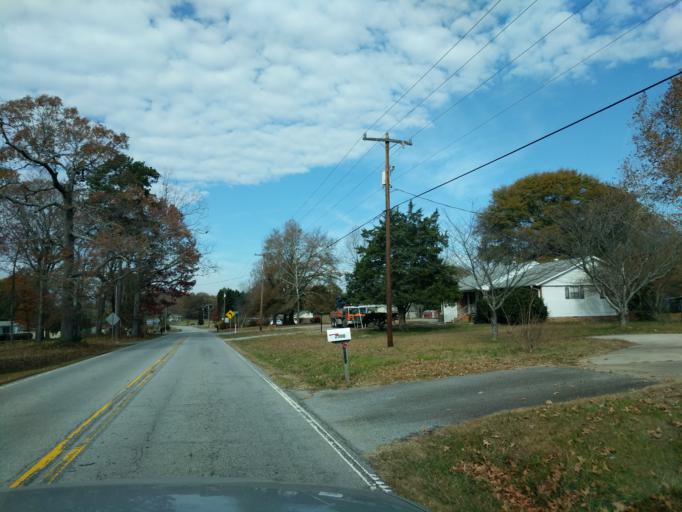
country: US
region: South Carolina
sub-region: Anderson County
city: Piedmont
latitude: 34.7157
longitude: -82.5136
